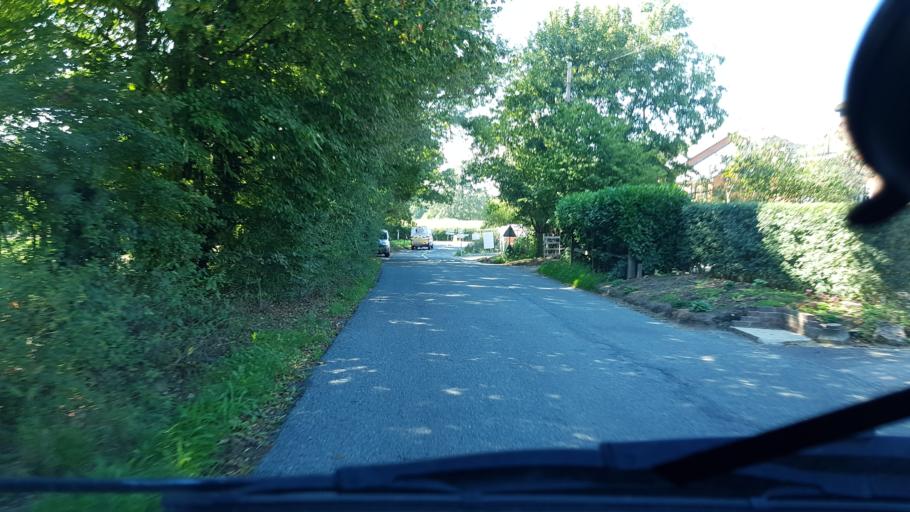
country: GB
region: England
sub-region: Surrey
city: Ockley
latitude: 51.1069
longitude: -0.3640
